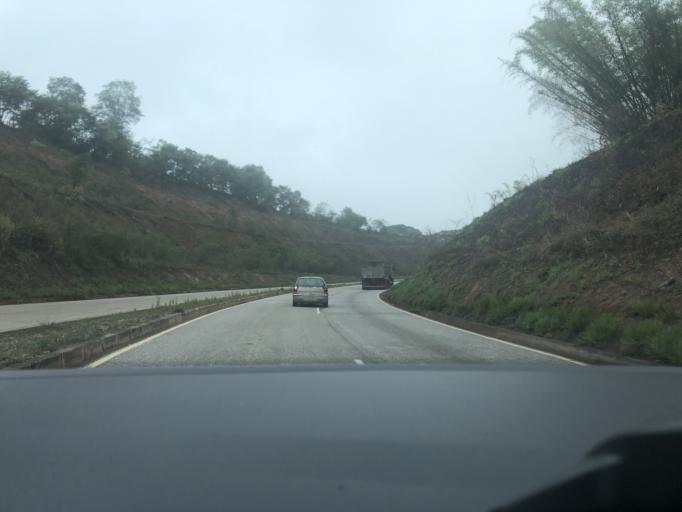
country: BR
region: Minas Gerais
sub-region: Congonhas
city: Congonhas
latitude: -20.5923
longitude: -43.9469
